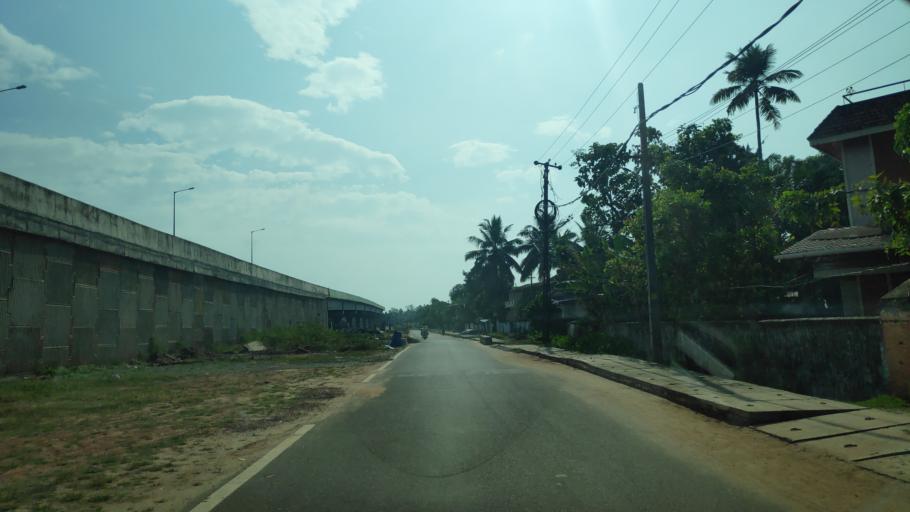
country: IN
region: Kerala
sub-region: Alappuzha
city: Alleppey
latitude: 9.5030
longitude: 76.3205
